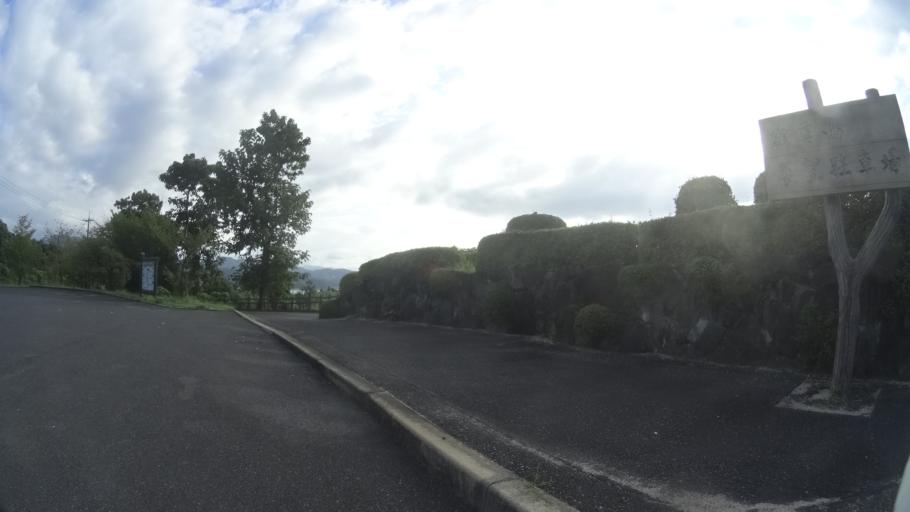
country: JP
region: Tottori
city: Kurayoshi
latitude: 35.4867
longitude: 133.8964
